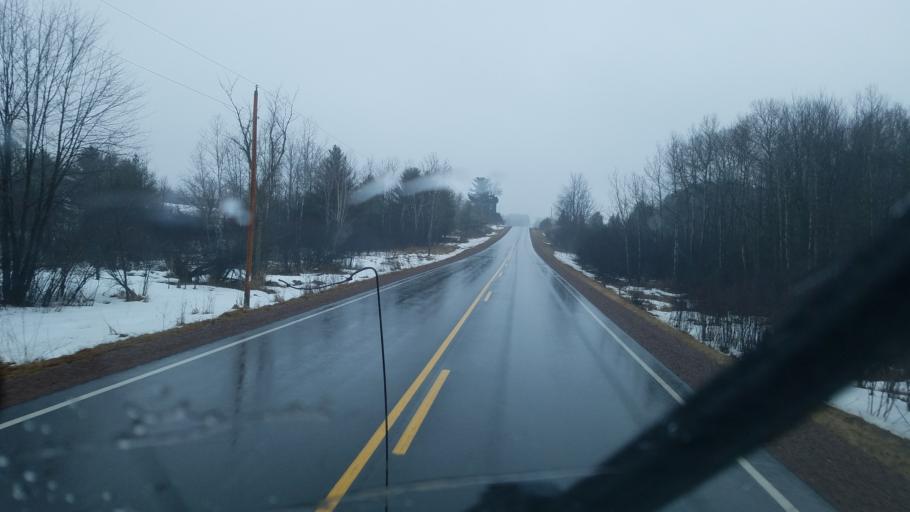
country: US
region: Wisconsin
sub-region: Wood County
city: Marshfield
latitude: 44.5759
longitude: -90.2996
